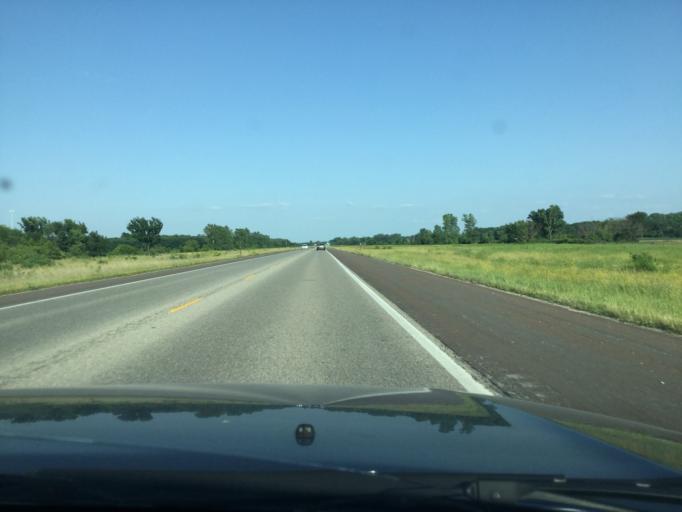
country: US
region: Kansas
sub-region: Douglas County
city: Lawrence
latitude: 38.9267
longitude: -95.2907
